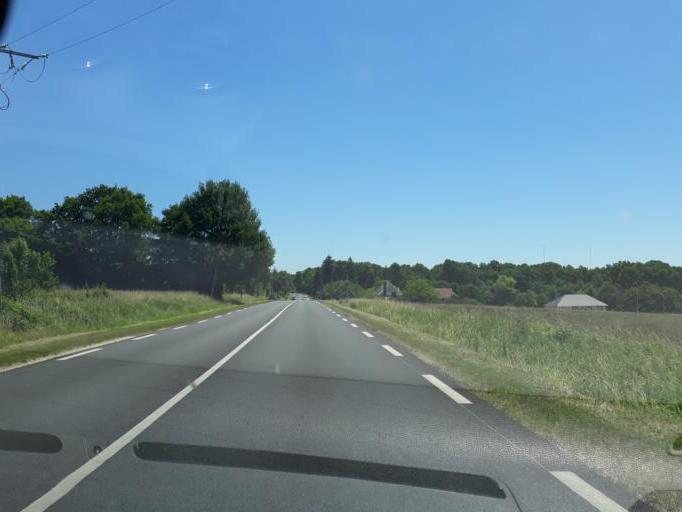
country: FR
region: Centre
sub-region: Departement du Cher
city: Vignoux-sur-Barangeon
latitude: 47.2087
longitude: 2.1472
